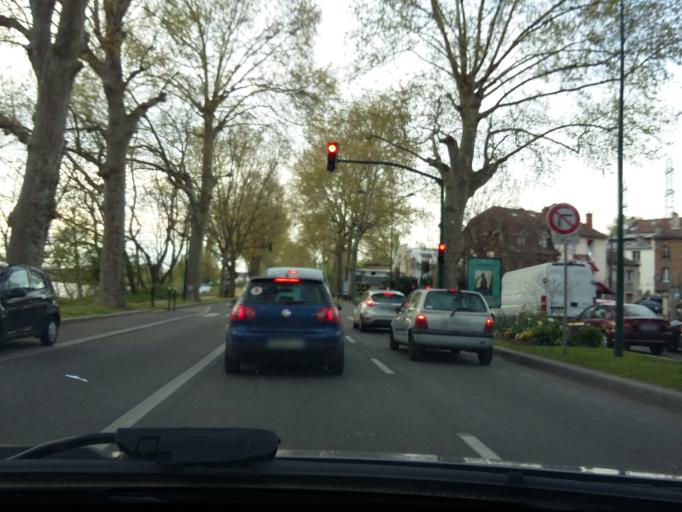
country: FR
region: Ile-de-France
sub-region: Departement de Seine-Saint-Denis
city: Villetaneuse
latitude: 48.9437
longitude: 2.3387
